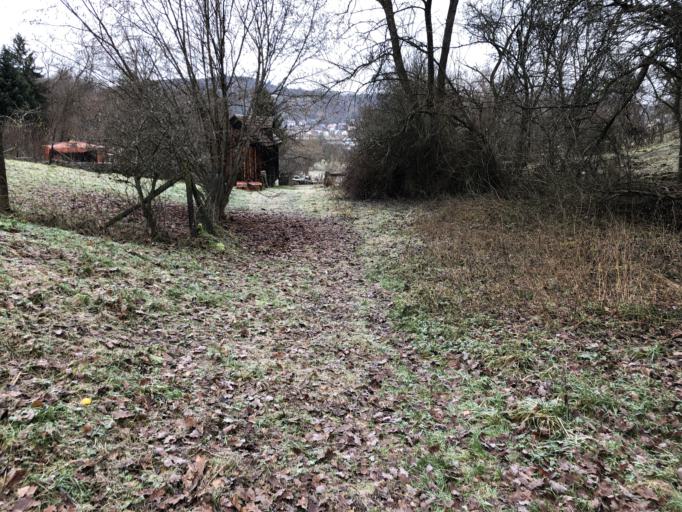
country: DE
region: Baden-Wuerttemberg
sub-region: Tuebingen Region
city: Tuebingen
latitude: 48.5150
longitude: 9.0287
